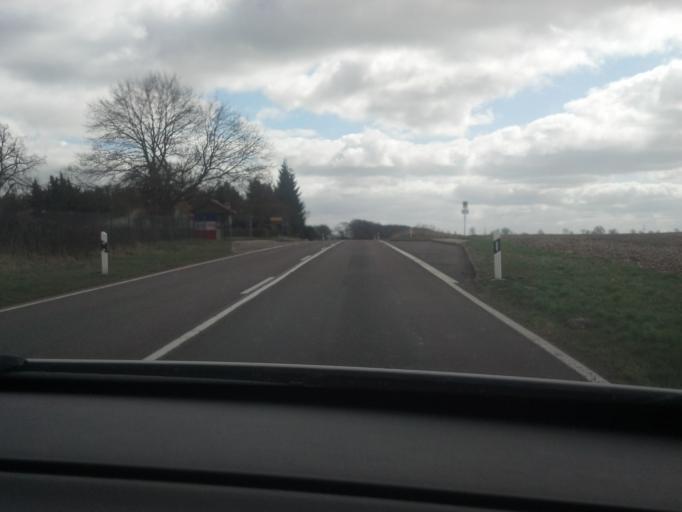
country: DE
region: Mecklenburg-Vorpommern
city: Plau am See
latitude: 53.3747
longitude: 12.3496
